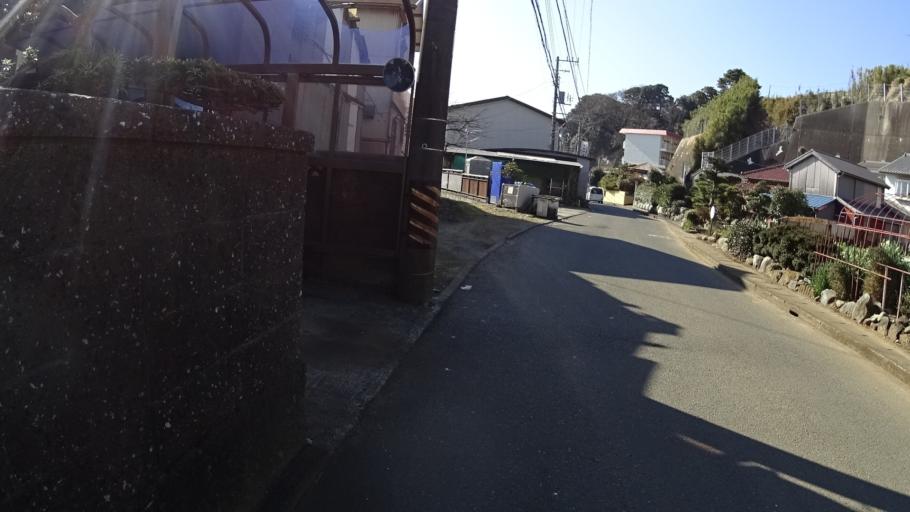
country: JP
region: Kanagawa
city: Miura
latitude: 35.1891
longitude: 139.6257
